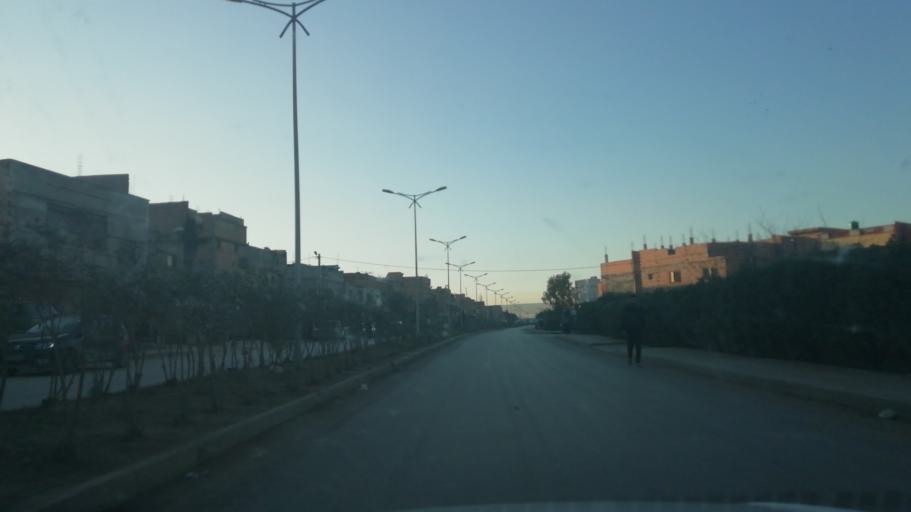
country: DZ
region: Oran
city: Es Senia
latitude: 35.6487
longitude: -0.5739
